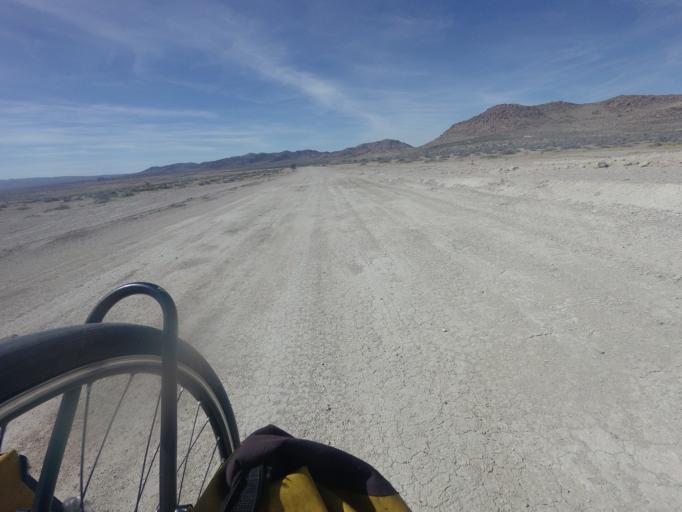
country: US
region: California
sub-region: San Bernardino County
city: Searles Valley
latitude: 35.6002
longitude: -117.3846
